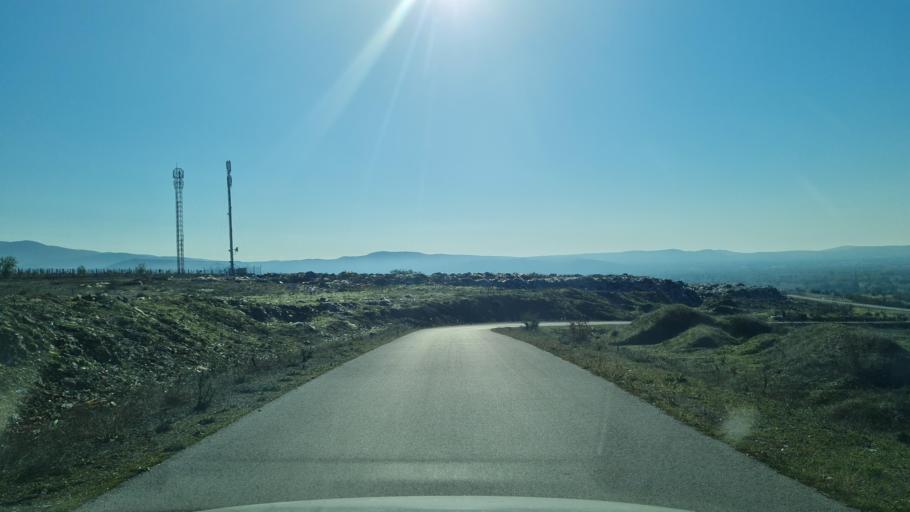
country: MK
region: Bogdanci
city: Bogdanci
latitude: 41.2003
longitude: 22.5612
